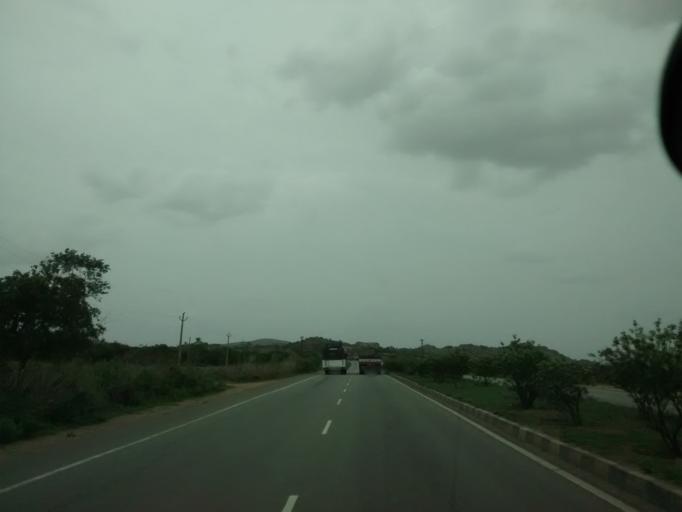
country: IN
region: Andhra Pradesh
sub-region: Kurnool
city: Ramapuram
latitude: 15.1983
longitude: 77.7074
